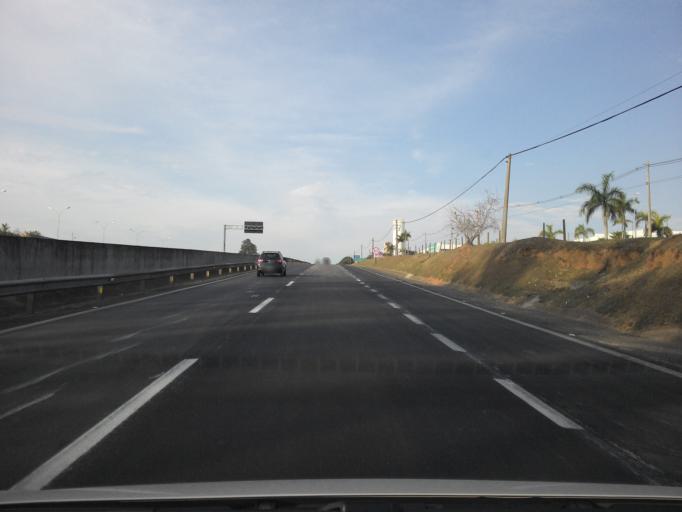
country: BR
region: Sao Paulo
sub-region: Hortolandia
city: Hortolandia
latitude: -22.9024
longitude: -47.2021
